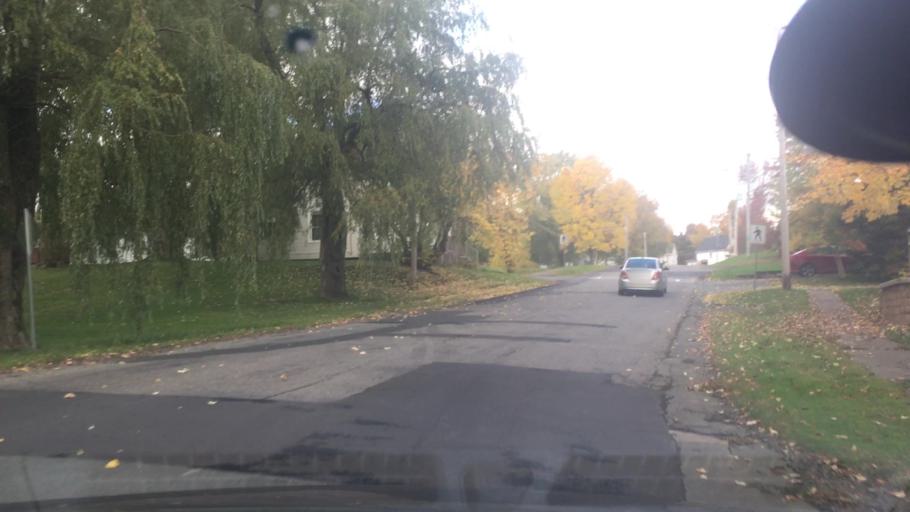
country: CA
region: Nova Scotia
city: Windsor
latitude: 44.9855
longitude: -64.1333
